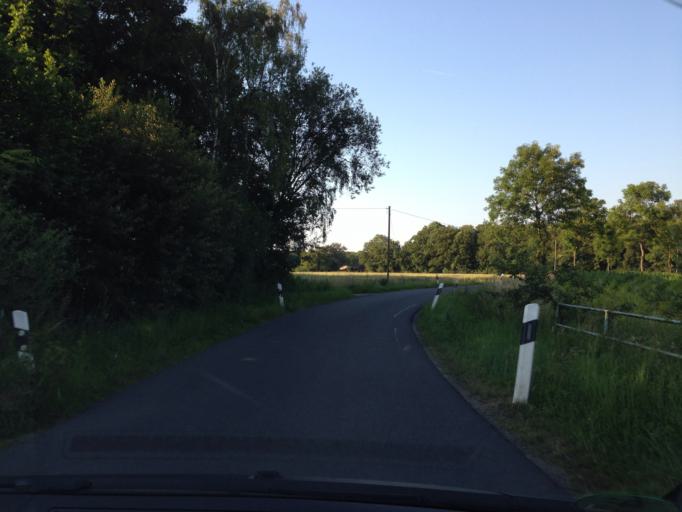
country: DE
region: North Rhine-Westphalia
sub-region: Regierungsbezirk Munster
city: Muenster
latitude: 52.0106
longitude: 7.5754
